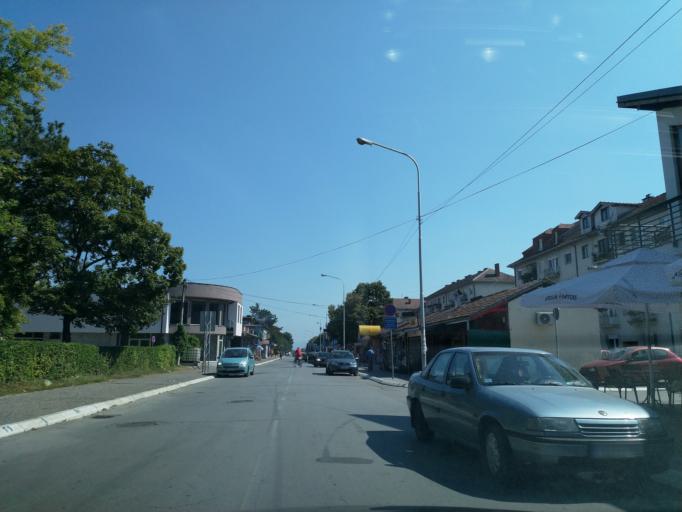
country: RS
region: Central Serbia
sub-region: Rasinski Okrug
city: Trstenik
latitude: 43.6186
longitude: 21.0049
